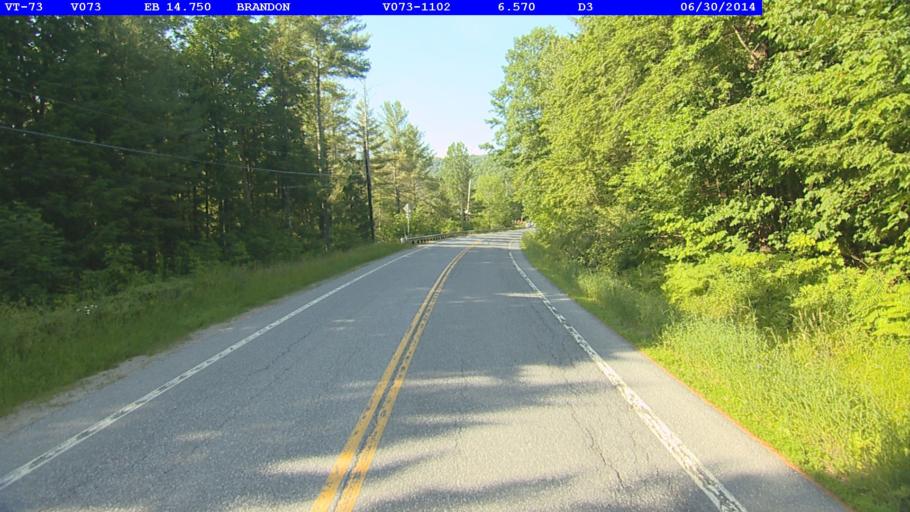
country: US
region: Vermont
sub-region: Rutland County
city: Brandon
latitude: 43.8338
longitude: -73.0433
